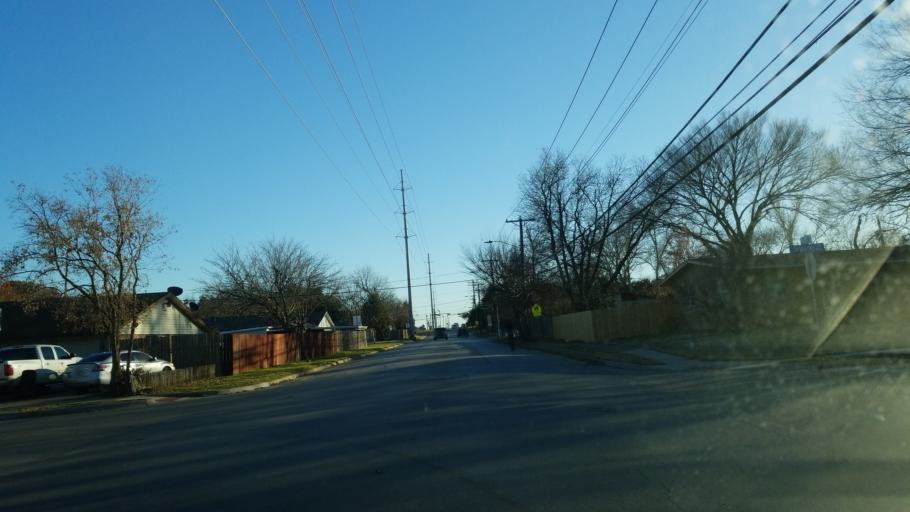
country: US
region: Texas
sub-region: Tarrant County
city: Arlington
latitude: 32.7235
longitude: -97.0717
